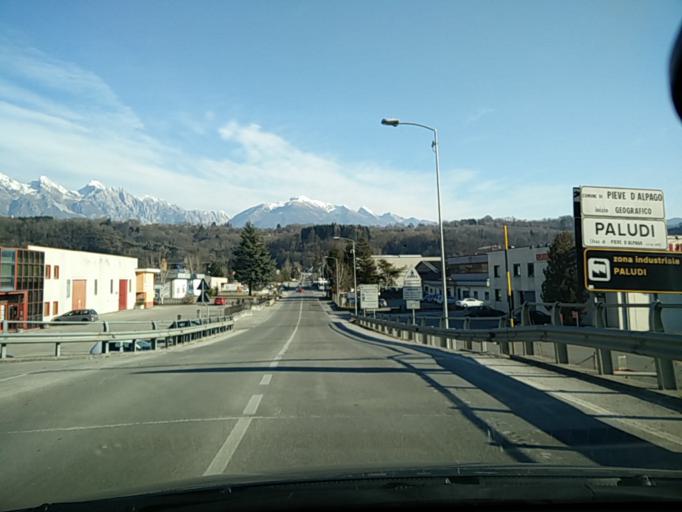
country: IT
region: Veneto
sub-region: Provincia di Belluno
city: Soccher-Paiane-Casan-Arsie
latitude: 46.1512
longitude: 12.3215
